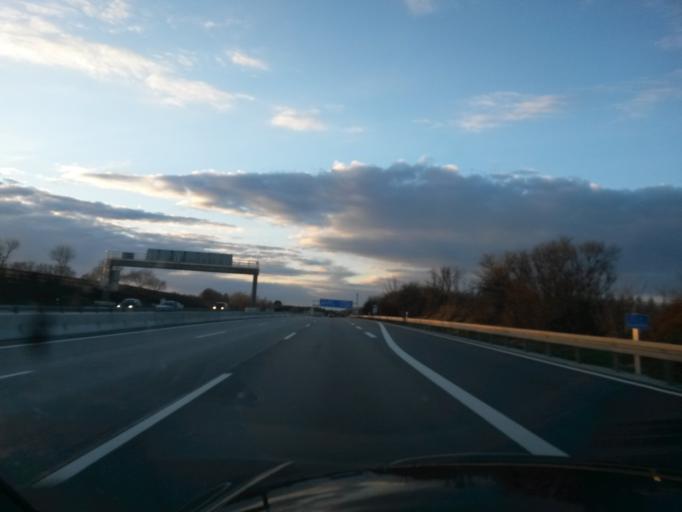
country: DE
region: Bavaria
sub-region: Upper Bavaria
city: Schweitenkirchen
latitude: 48.5020
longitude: 11.5921
